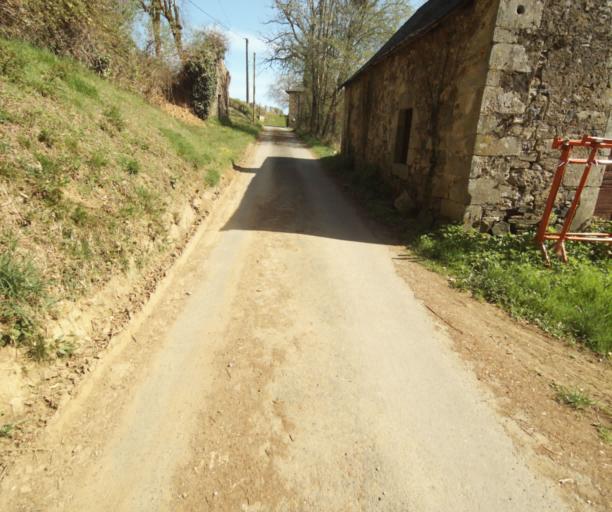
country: FR
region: Limousin
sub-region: Departement de la Correze
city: Naves
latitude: 45.3511
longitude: 1.7819
